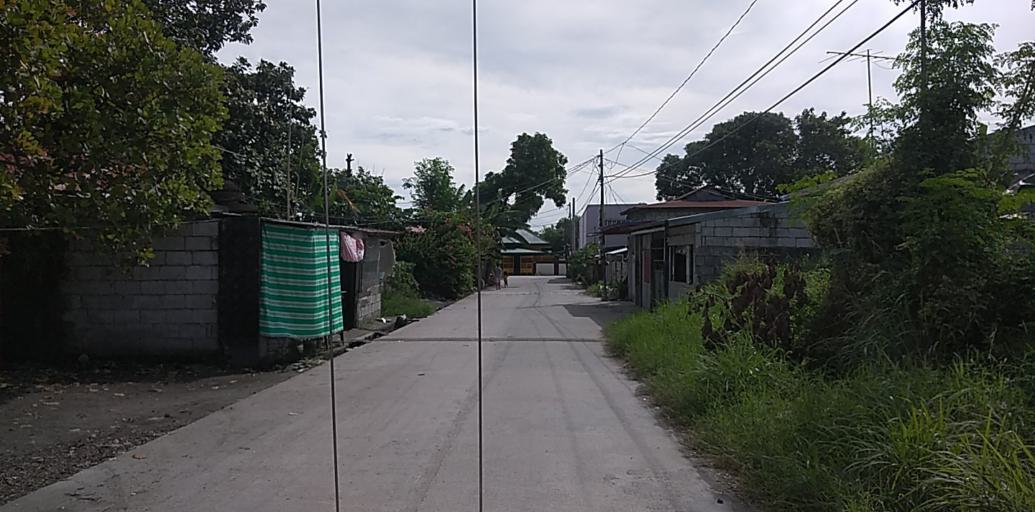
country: PH
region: Central Luzon
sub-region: Province of Pampanga
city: Angeles City
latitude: 15.1284
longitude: 120.5635
